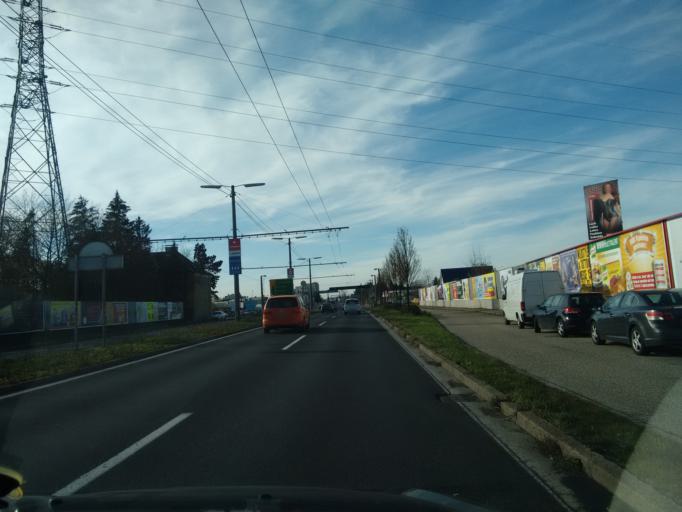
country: AT
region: Upper Austria
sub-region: Politischer Bezirk Linz-Land
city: Leonding
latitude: 48.2486
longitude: 14.2671
